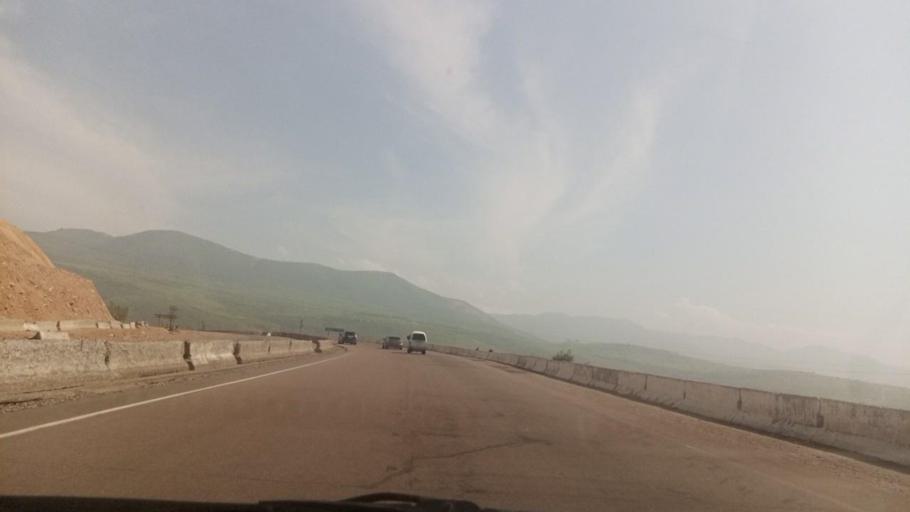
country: UZ
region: Toshkent
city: Angren
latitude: 41.0725
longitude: 70.2354
